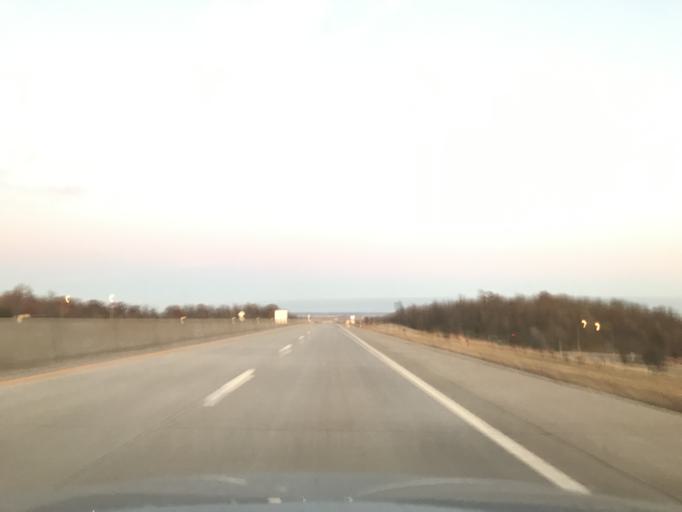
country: US
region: Missouri
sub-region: Marion County
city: Hannibal
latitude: 39.7165
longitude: -91.3756
